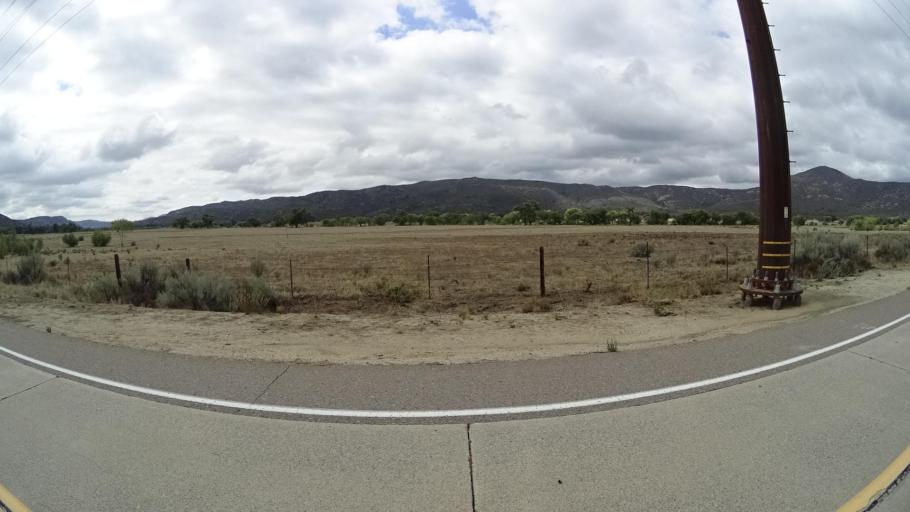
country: US
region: California
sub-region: San Diego County
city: Pine Valley
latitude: 32.7442
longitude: -116.4817
